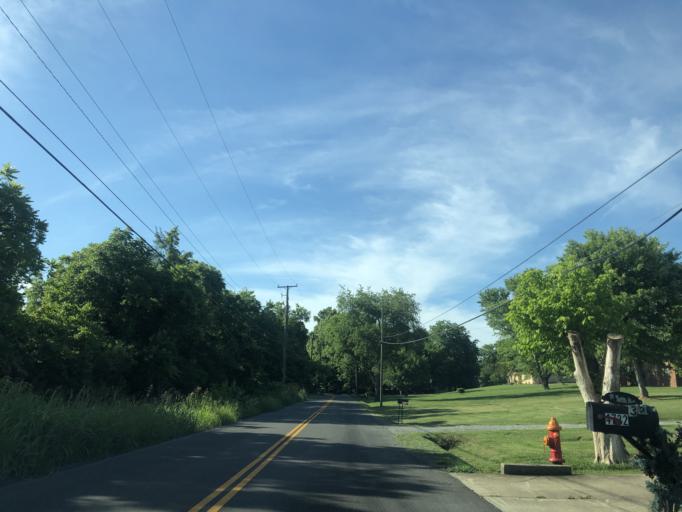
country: US
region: Tennessee
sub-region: Davidson County
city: Nashville
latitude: 36.2193
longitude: -86.8500
